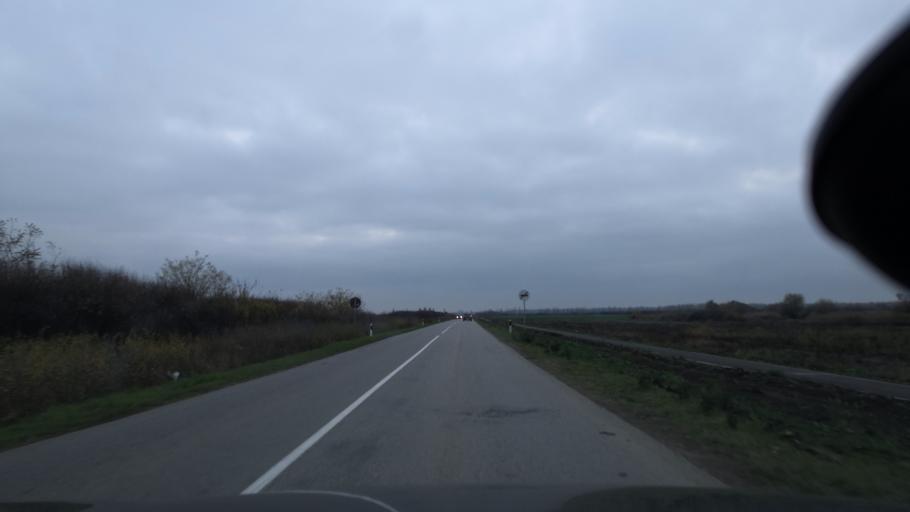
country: RS
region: Autonomna Pokrajina Vojvodina
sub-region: Severnobanatski Okrug
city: Novi Knezevac
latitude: 46.0904
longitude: 20.1098
